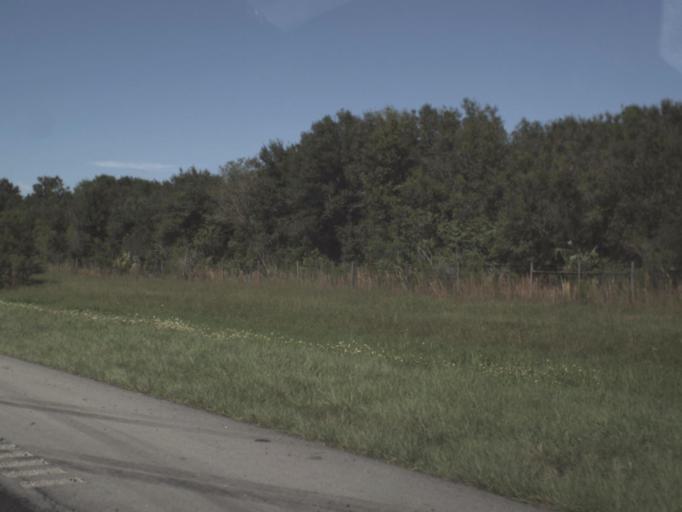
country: US
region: Florida
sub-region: Lee County
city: Suncoast Estates
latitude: 26.7485
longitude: -81.8603
